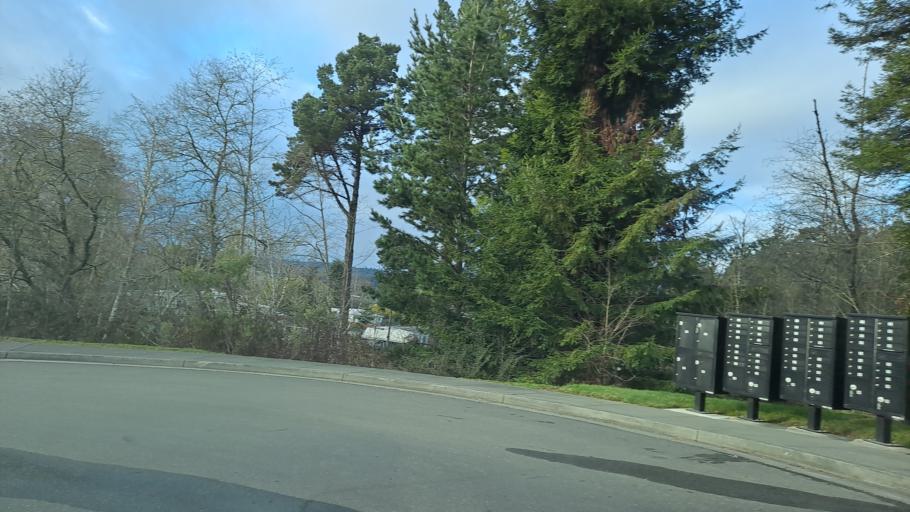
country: US
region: California
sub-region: Humboldt County
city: Fortuna
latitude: 40.5771
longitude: -124.1273
